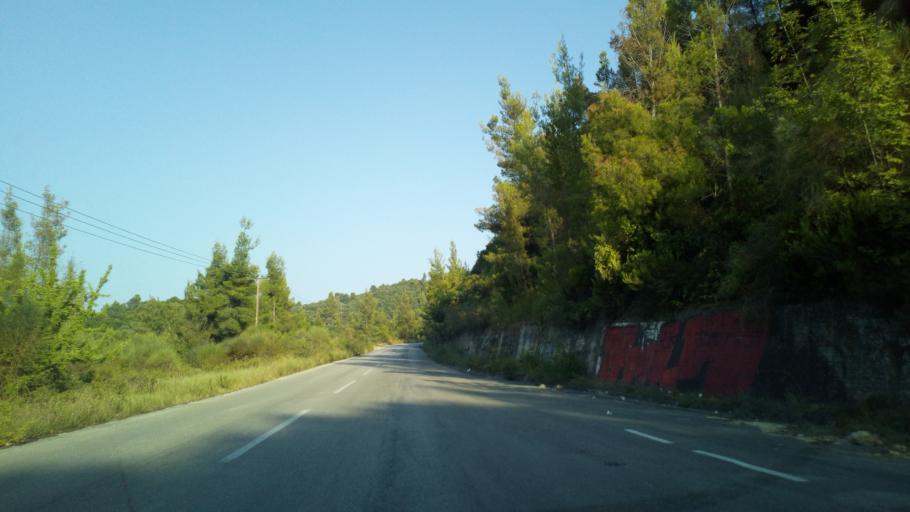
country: GR
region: Central Macedonia
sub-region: Nomos Chalkidikis
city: Neos Marmaras
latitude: 40.1624
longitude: 23.8693
